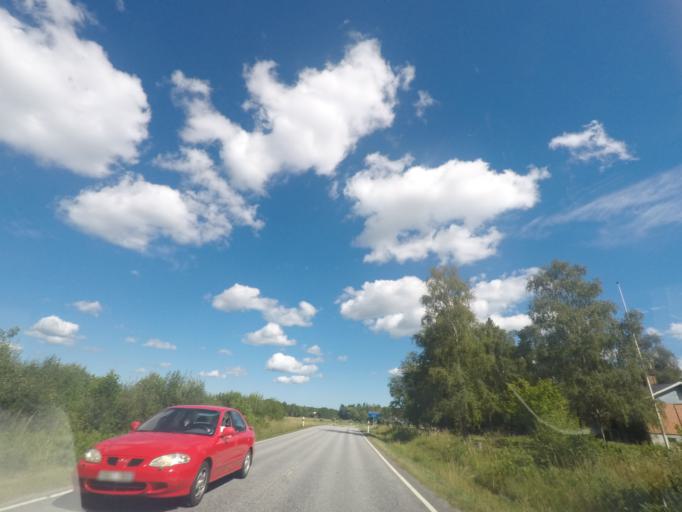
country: SE
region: Stockholm
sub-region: Norrtalje Kommun
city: Hallstavik
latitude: 59.9494
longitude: 18.7600
